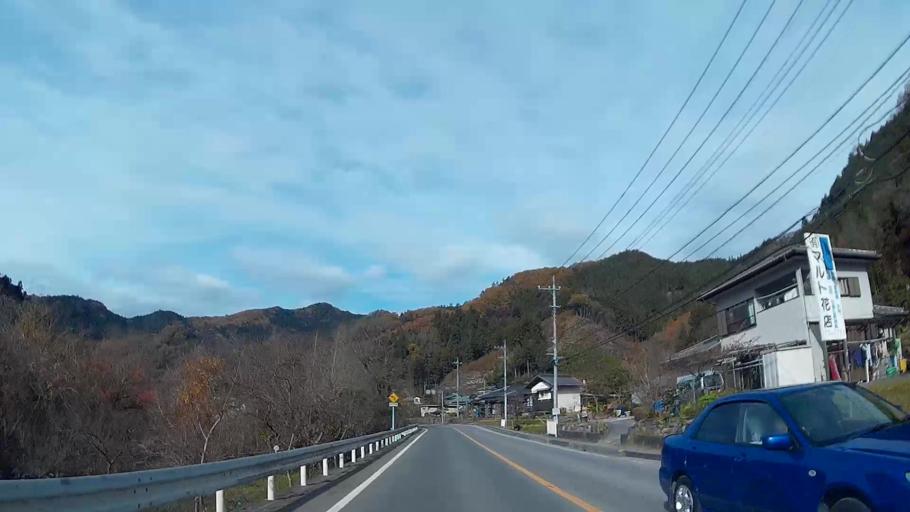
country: JP
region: Saitama
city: Chichibu
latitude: 36.0490
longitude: 139.0125
